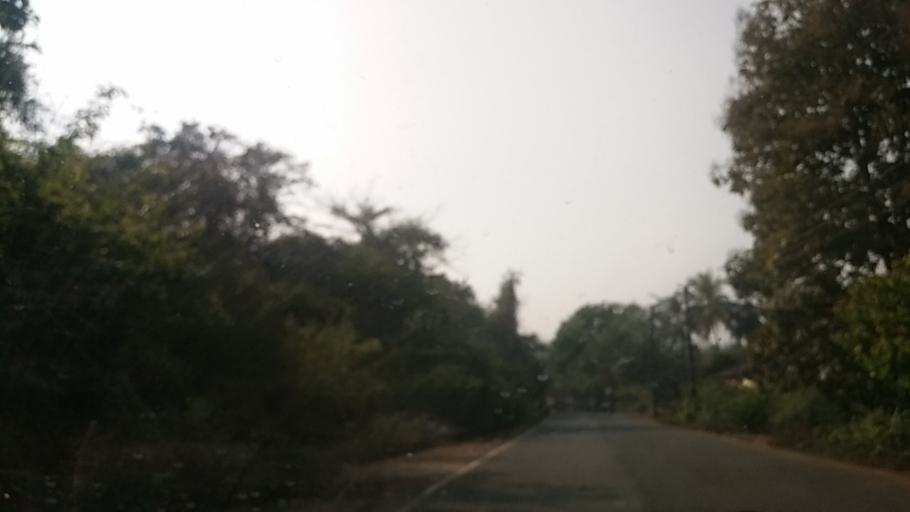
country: IN
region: Goa
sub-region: North Goa
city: Pernem
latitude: 15.7163
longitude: 73.8021
